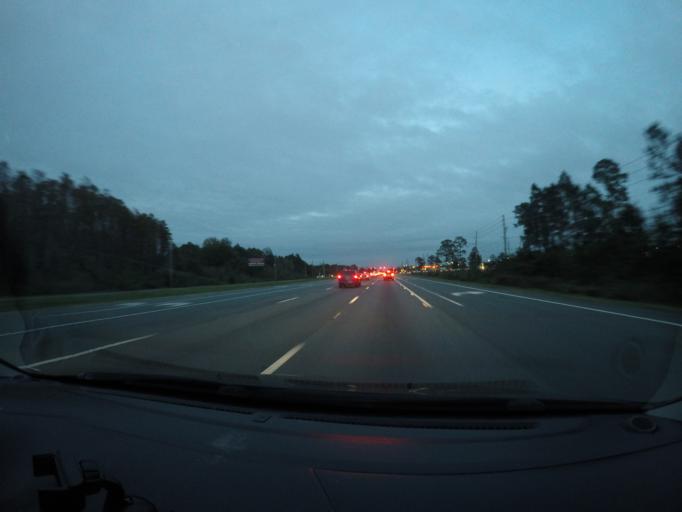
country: US
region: Florida
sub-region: Orange County
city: Tangelo Park
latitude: 28.4502
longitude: -81.4304
